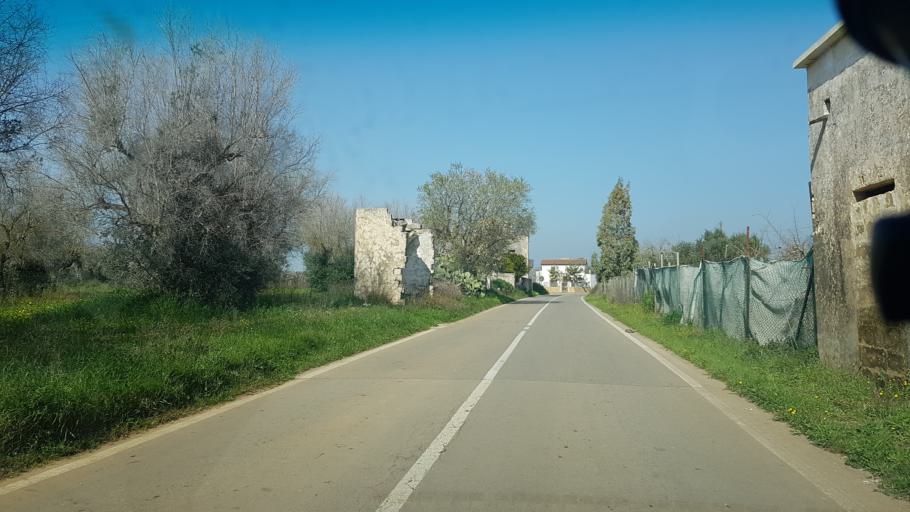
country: IT
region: Apulia
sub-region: Provincia di Lecce
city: Squinzano
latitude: 40.4498
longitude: 18.0408
